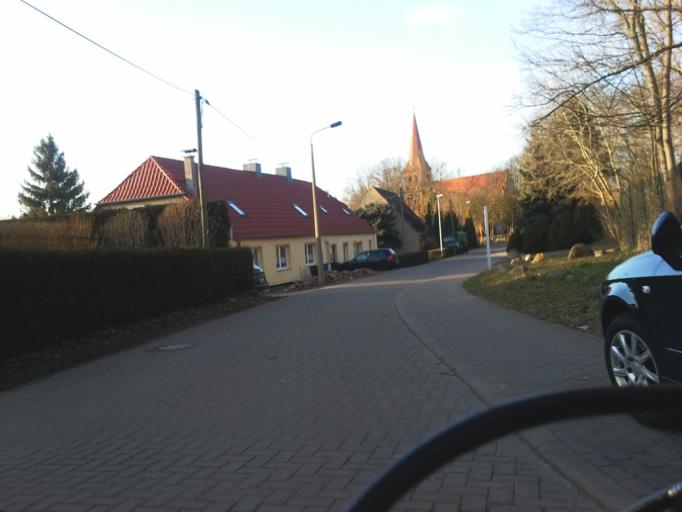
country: DE
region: Mecklenburg-Vorpommern
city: Dierkow-West
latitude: 54.1173
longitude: 12.1387
